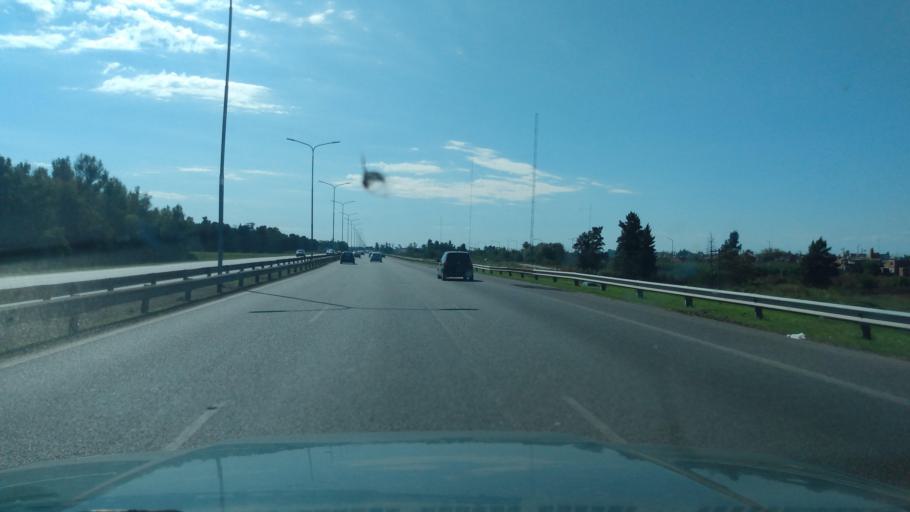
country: AR
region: Buenos Aires
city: Hurlingham
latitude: -34.5470
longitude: -58.6041
